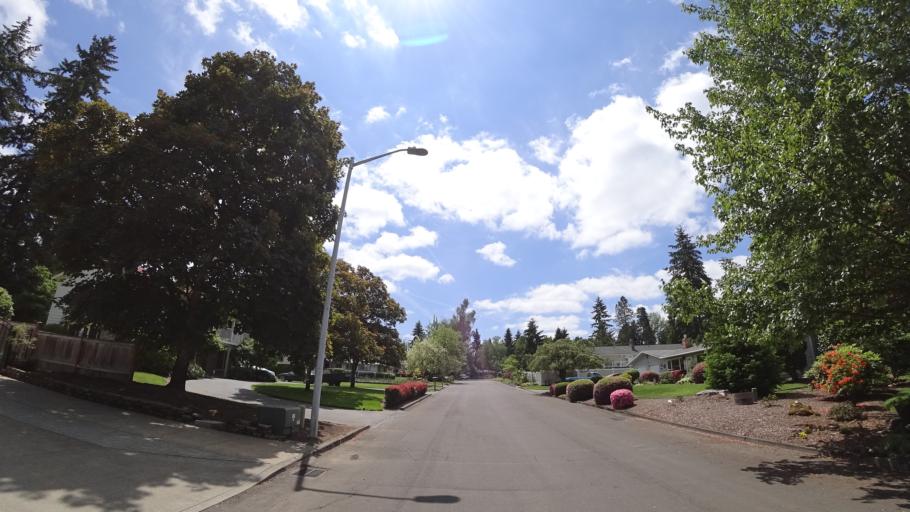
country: US
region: Oregon
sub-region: Washington County
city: Tigard
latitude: 45.4329
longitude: -122.7958
